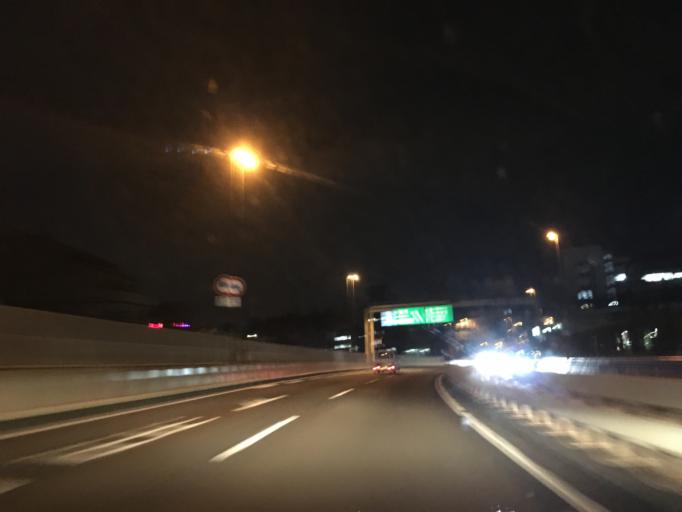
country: JP
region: Tokyo
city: Tokyo
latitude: 35.6797
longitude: 139.7227
